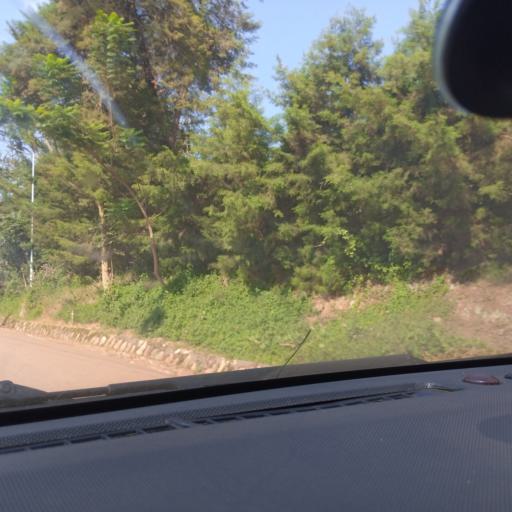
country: UG
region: Central Region
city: Masaka
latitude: -0.3339
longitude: 31.7371
